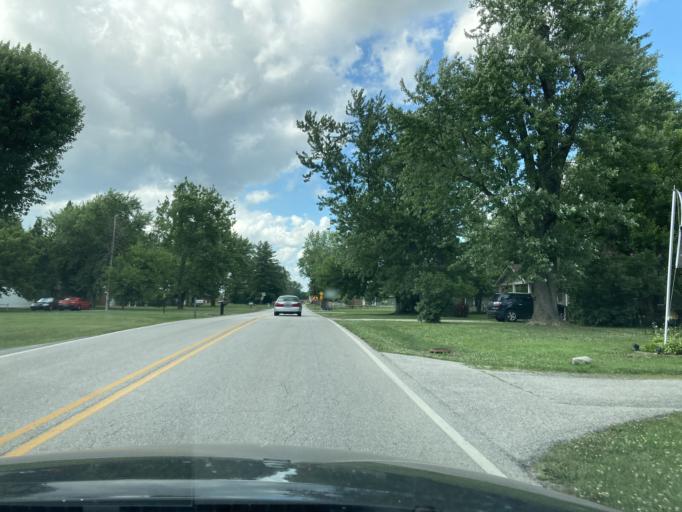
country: US
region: Indiana
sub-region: Marion County
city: Meridian Hills
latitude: 39.8656
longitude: -86.2121
